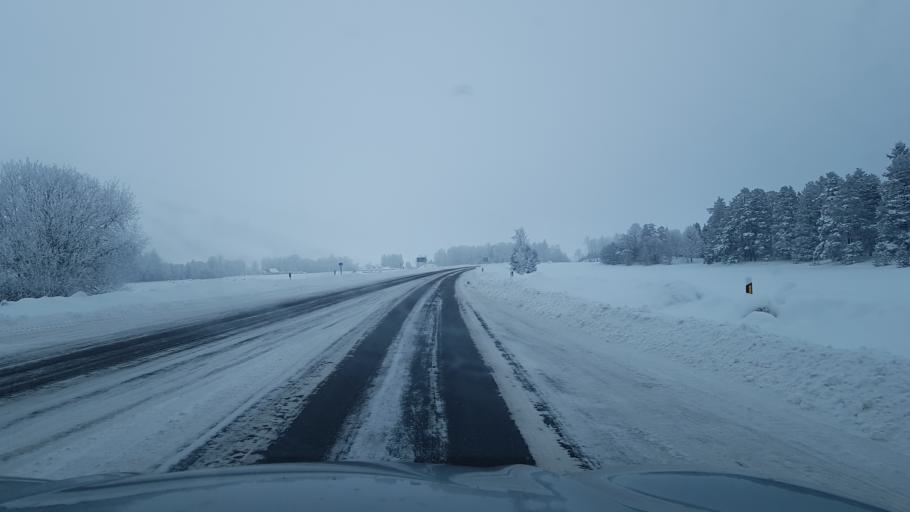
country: EE
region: Ida-Virumaa
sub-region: Johvi vald
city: Johvi
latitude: 59.2279
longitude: 27.3391
